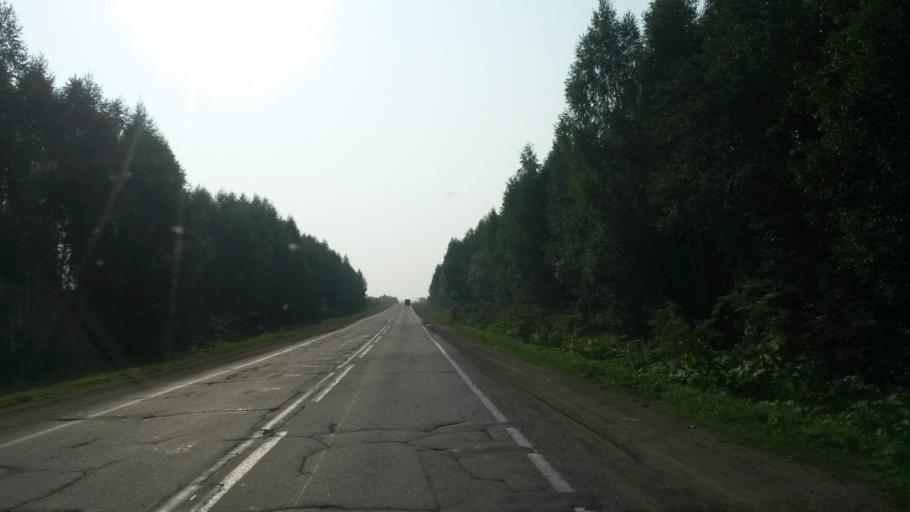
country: RU
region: Jaroslavl
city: Dubki
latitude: 57.2500
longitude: 40.1232
